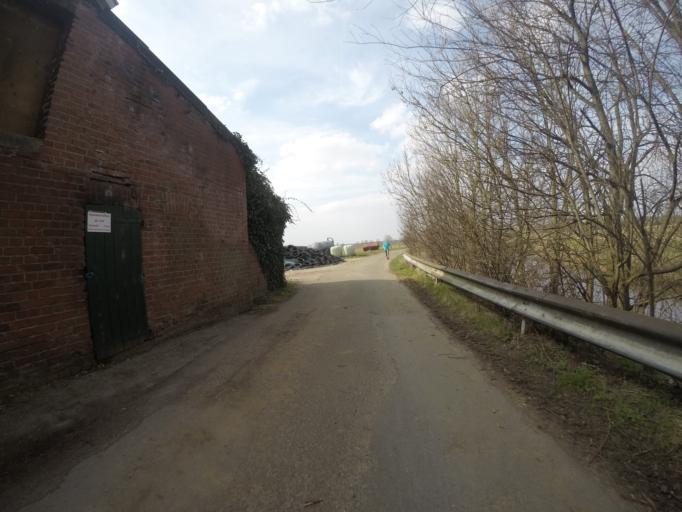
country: DE
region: North Rhine-Westphalia
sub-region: Regierungsbezirk Munster
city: Rhede
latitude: 51.8210
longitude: 6.6852
